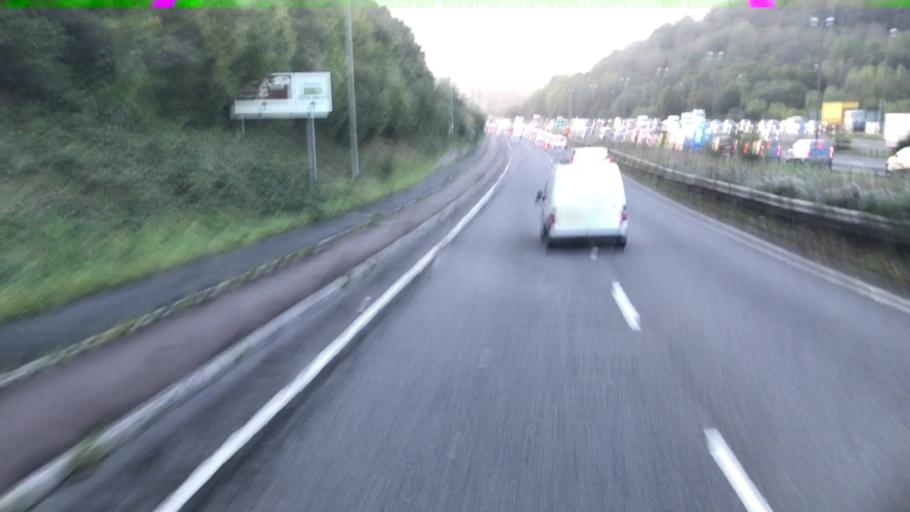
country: GB
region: England
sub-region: Devon
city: Plympton
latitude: 50.3951
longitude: -4.0952
